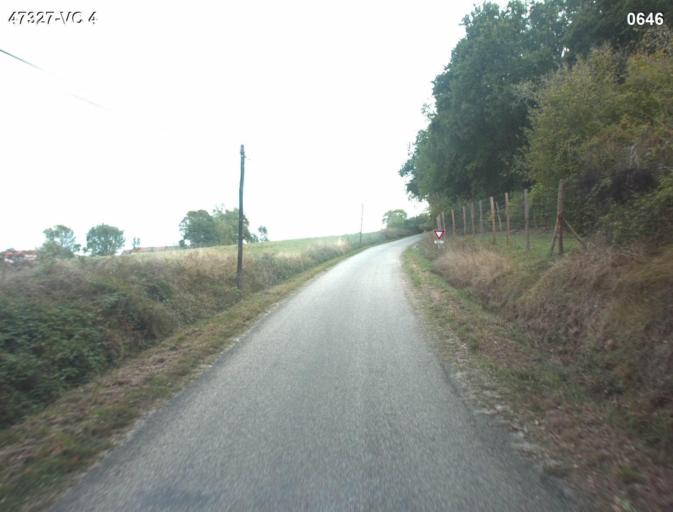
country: FR
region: Aquitaine
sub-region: Departement du Lot-et-Garonne
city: Barbaste
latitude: 44.2098
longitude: 0.2588
